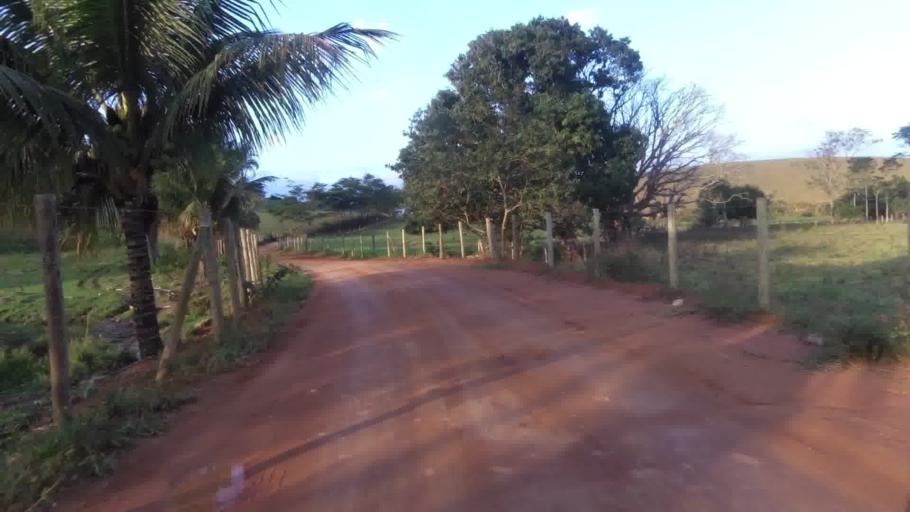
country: BR
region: Espirito Santo
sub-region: Guarapari
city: Guarapari
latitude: -20.6803
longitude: -40.6264
